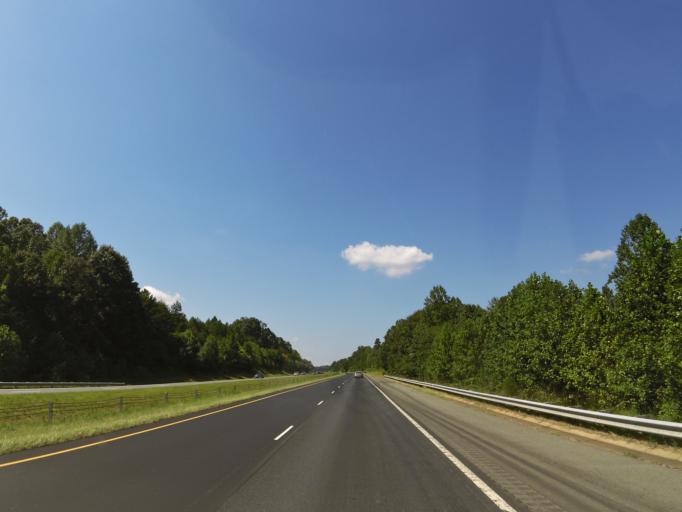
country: US
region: North Carolina
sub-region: Lincoln County
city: Lincolnton
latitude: 35.4407
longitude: -81.2109
